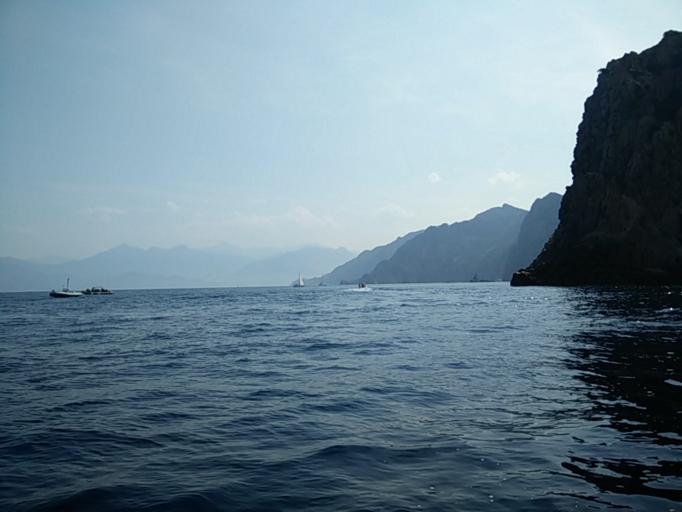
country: FR
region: Corsica
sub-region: Departement de la Corse-du-Sud
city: Cargese
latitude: 42.2406
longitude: 8.5475
